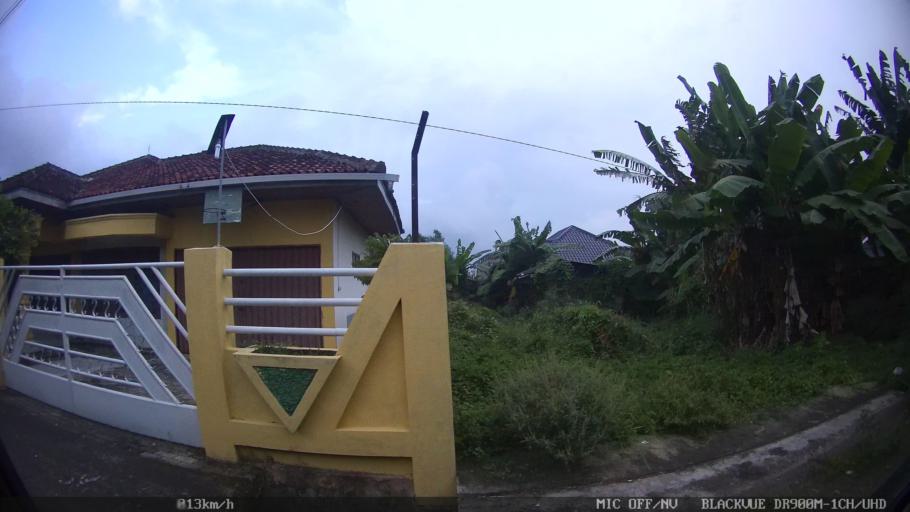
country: ID
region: Lampung
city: Bandarlampung
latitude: -5.4198
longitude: 105.2740
